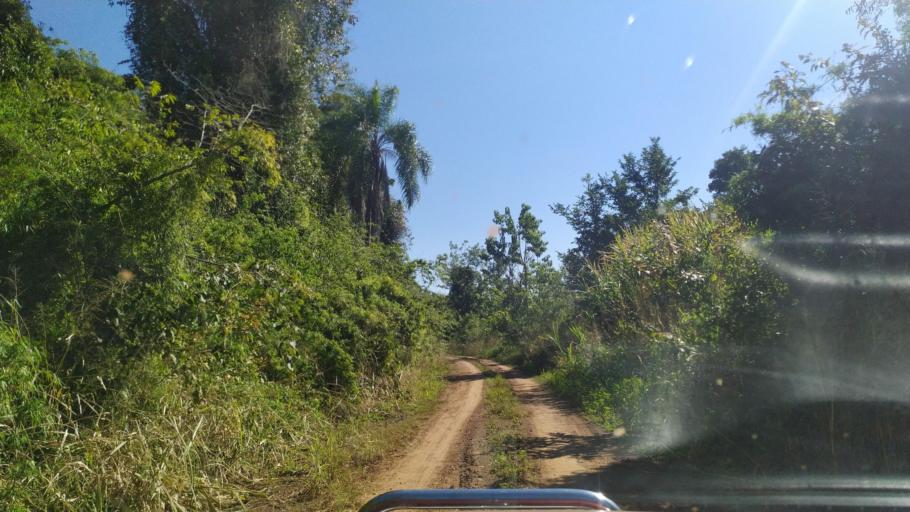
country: AR
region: Misiones
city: El Alcazar
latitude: -26.7588
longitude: -54.5881
